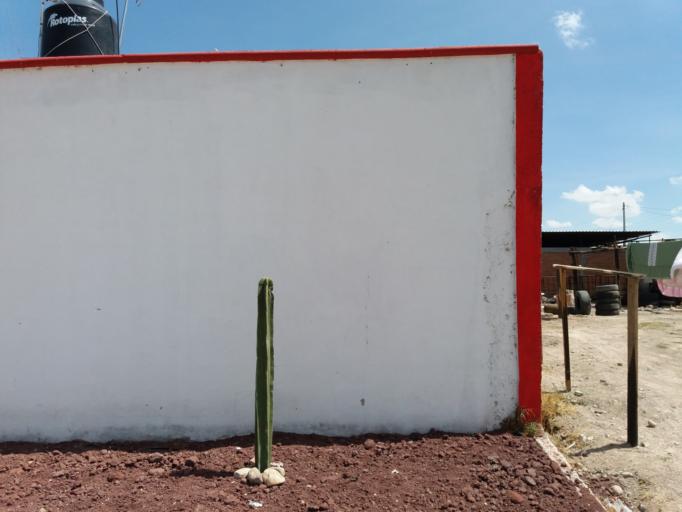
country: MX
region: Aguascalientes
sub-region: Aguascalientes
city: San Sebastian [Fraccionamiento]
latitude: 21.8114
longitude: -102.2942
